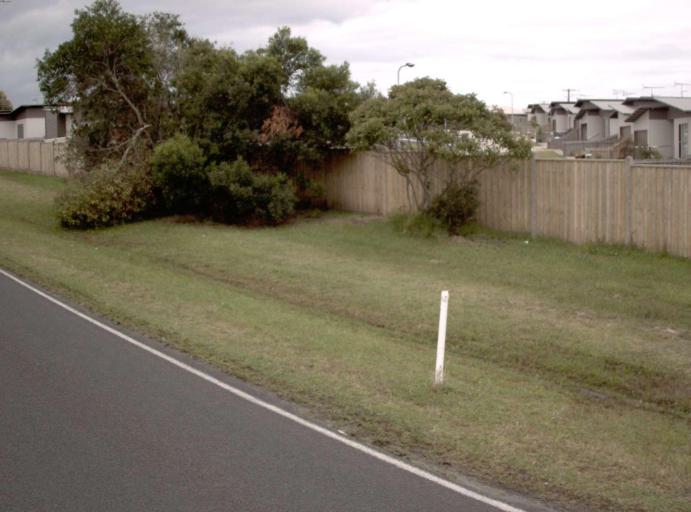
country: AU
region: Victoria
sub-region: Bass Coast
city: North Wonthaggi
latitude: -38.5990
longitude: 145.6051
